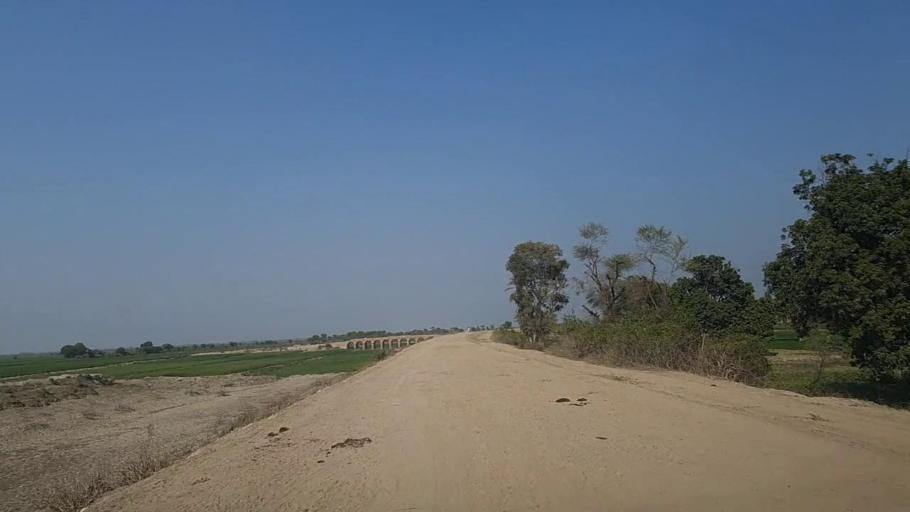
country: PK
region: Sindh
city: Naushahro Firoz
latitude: 26.8517
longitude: 67.9586
